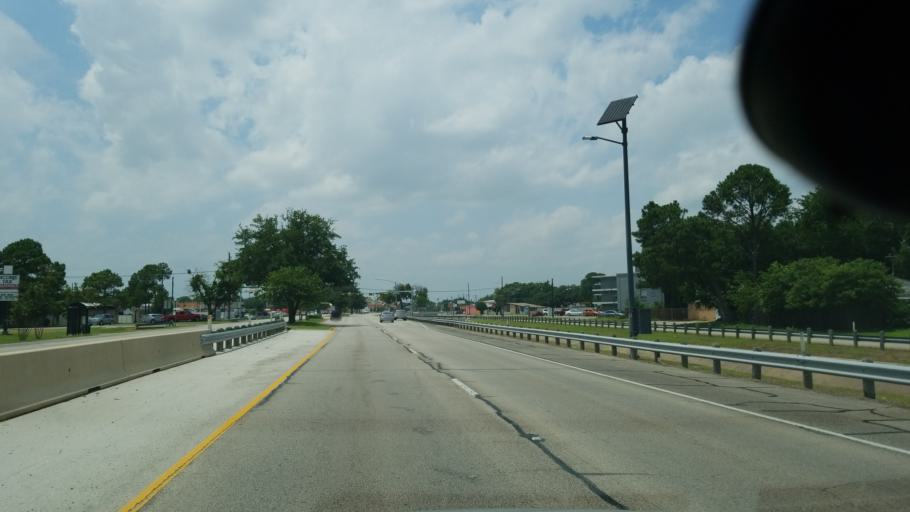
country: US
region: Texas
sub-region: Dallas County
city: Irving
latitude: 32.8171
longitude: -96.9622
